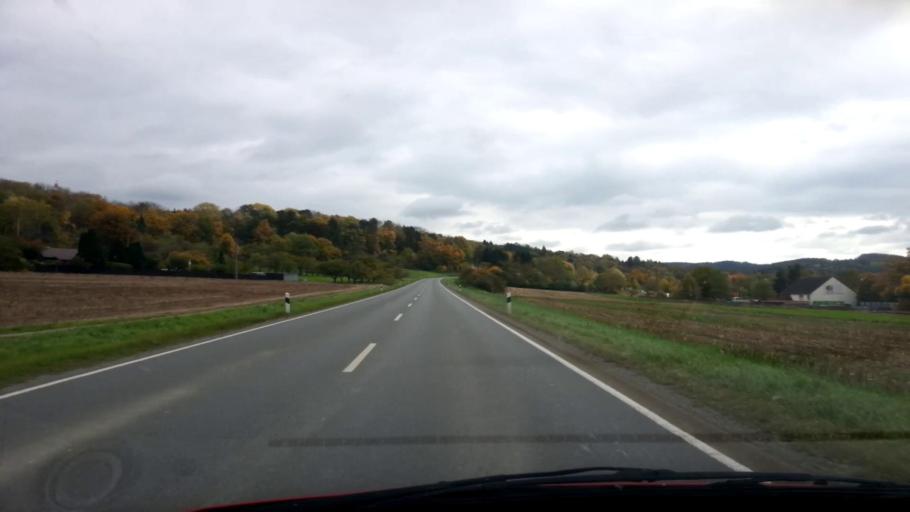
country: DE
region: Bavaria
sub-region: Upper Franconia
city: Bindlach
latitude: 49.9633
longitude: 11.6315
